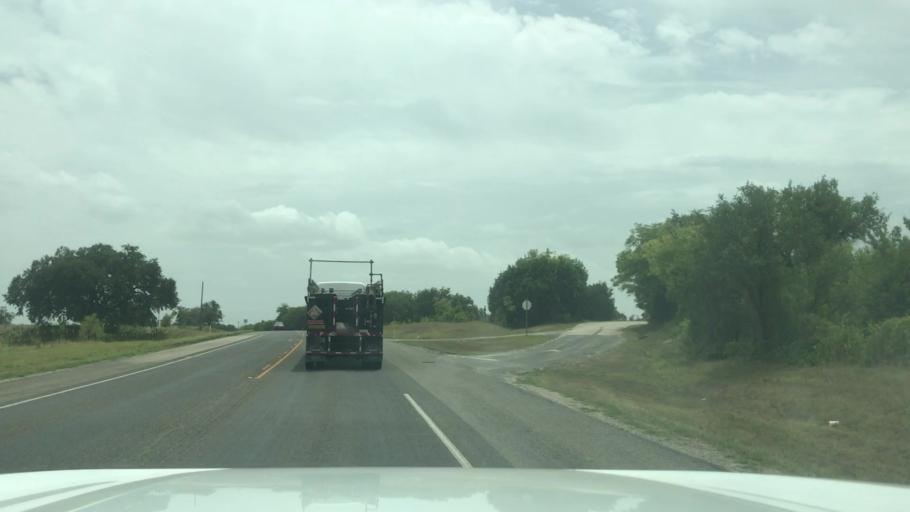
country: US
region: Texas
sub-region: Bosque County
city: Clifton
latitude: 31.7072
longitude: -97.5452
